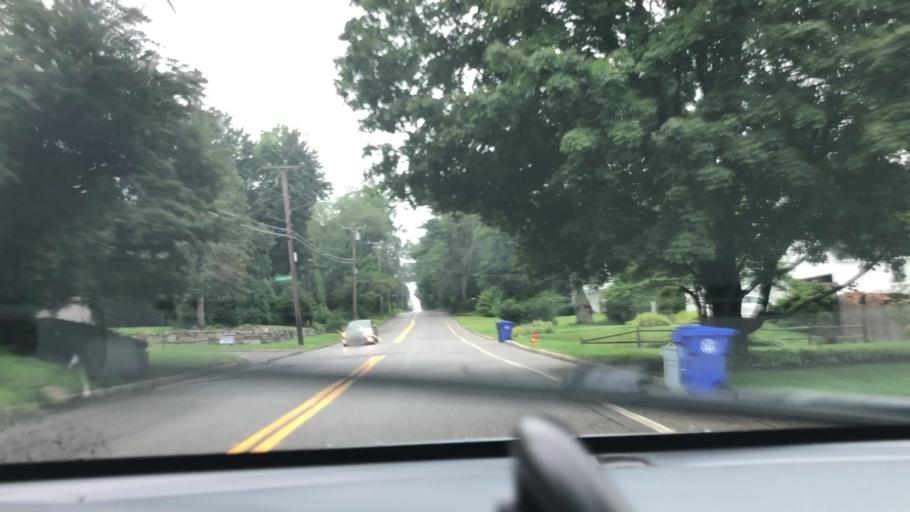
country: US
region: New Hampshire
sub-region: Merrimack County
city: South Hooksett
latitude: 43.0254
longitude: -71.4623
